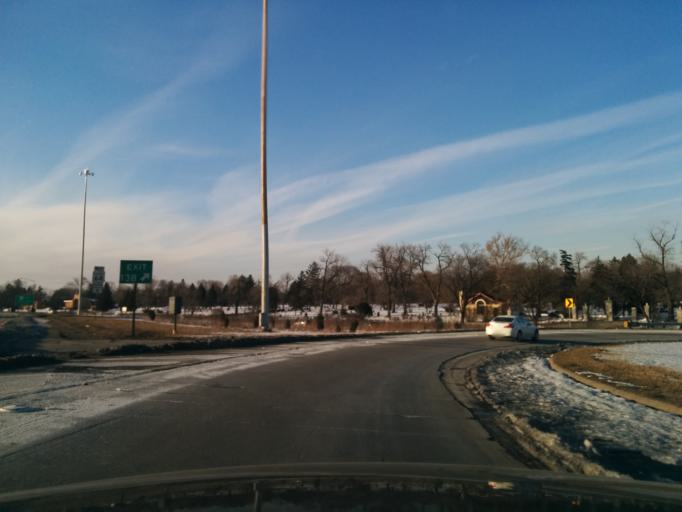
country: US
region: Illinois
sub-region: DuPage County
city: Elmhurst
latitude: 41.9070
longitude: -87.9239
